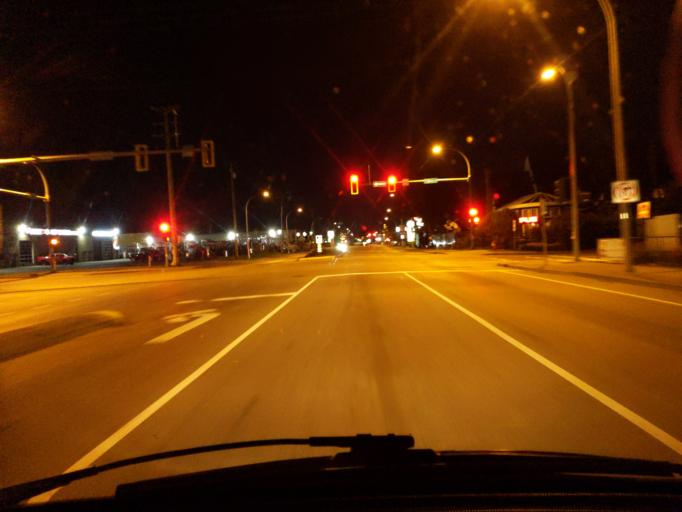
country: CA
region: British Columbia
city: Walnut Grove
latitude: 49.1770
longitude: -122.6689
